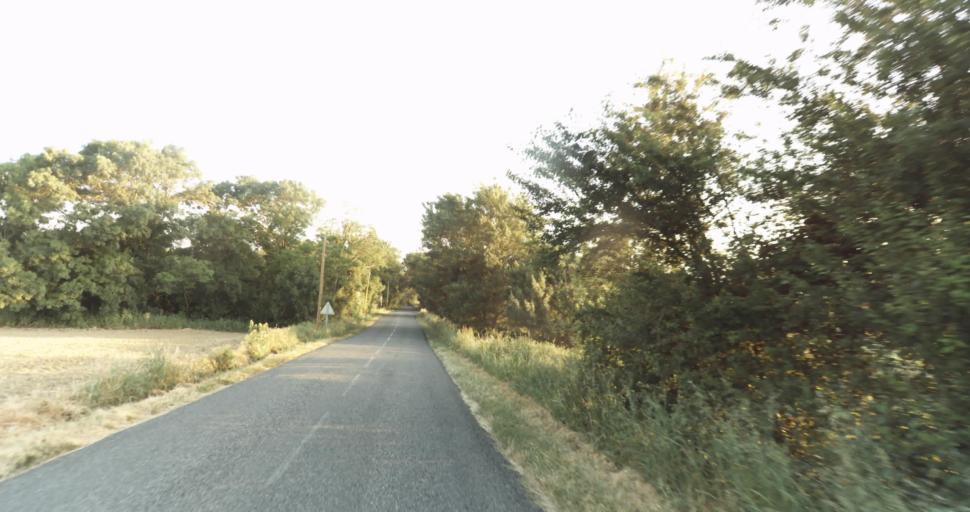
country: FR
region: Midi-Pyrenees
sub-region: Departement du Gers
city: Pujaudran
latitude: 43.6139
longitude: 1.1581
